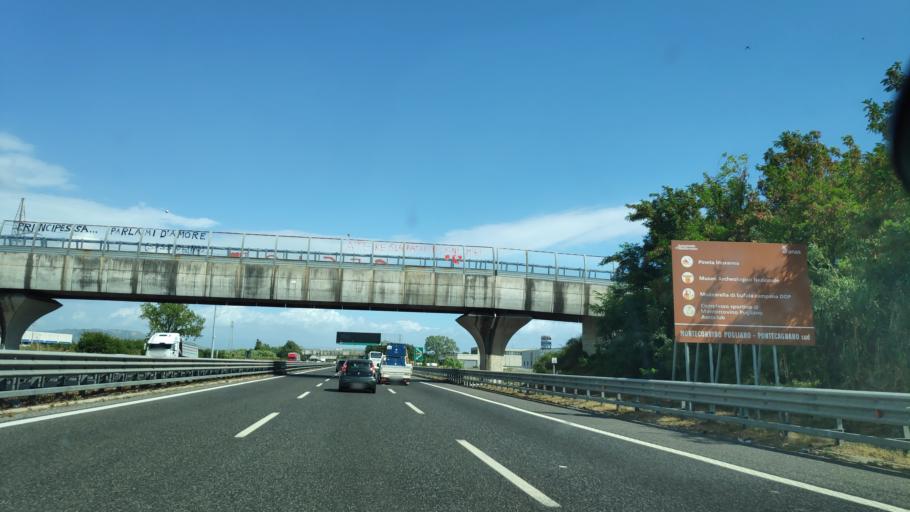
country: IT
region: Campania
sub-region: Provincia di Salerno
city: Sant'Antonio
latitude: 40.6389
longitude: 14.9020
